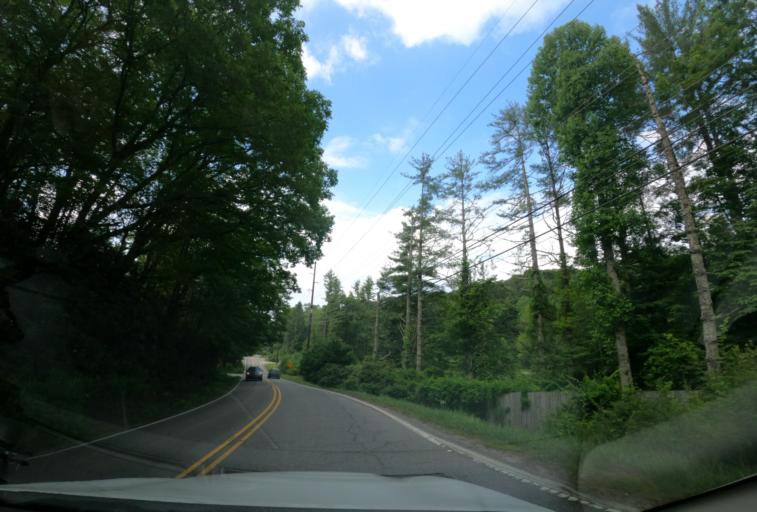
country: US
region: North Carolina
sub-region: Macon County
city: Franklin
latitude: 35.0828
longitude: -83.1890
